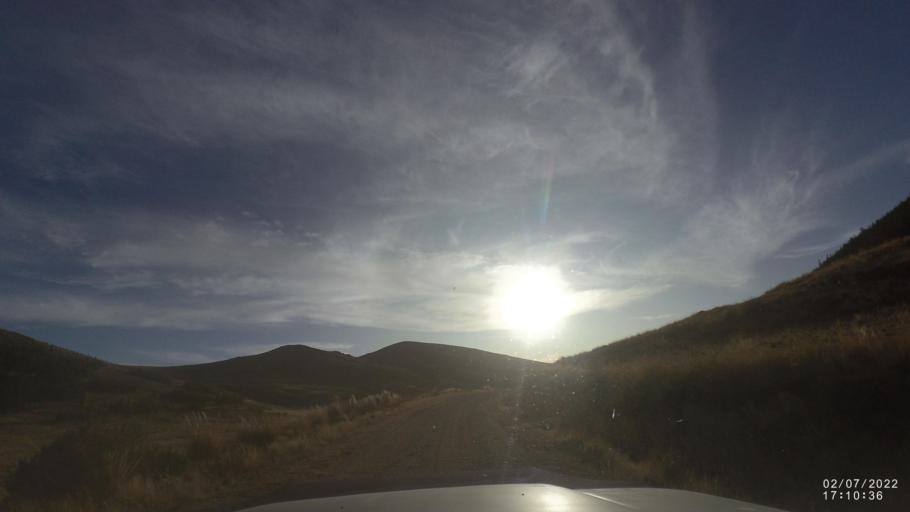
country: BO
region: Cochabamba
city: Irpa Irpa
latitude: -17.8958
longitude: -66.5594
